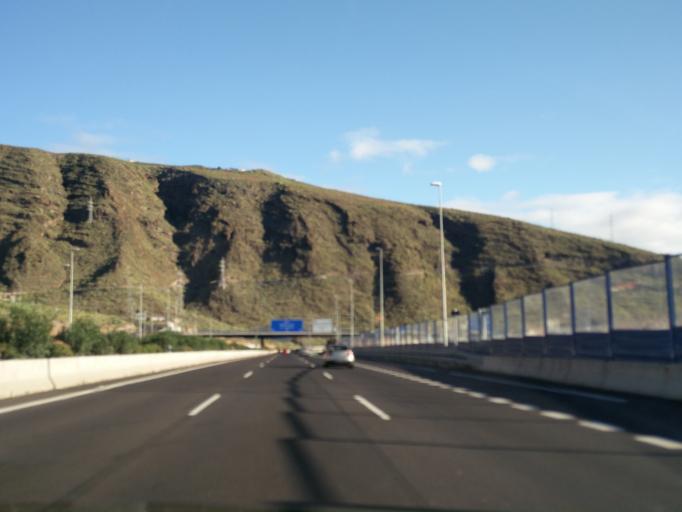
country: ES
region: Canary Islands
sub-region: Provincia de Santa Cruz de Tenerife
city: Candelaria
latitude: 28.3791
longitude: -16.3642
